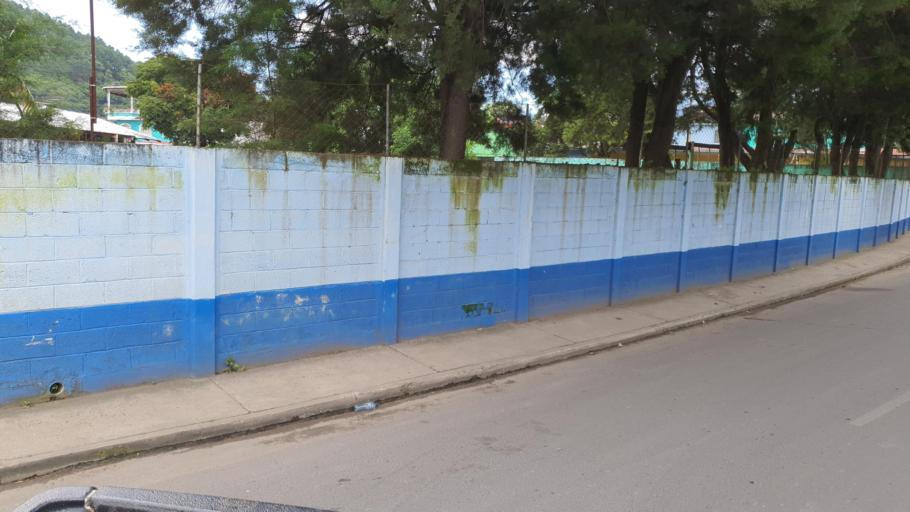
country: GT
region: Guatemala
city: Villa Canales
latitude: 14.4765
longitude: -90.5371
